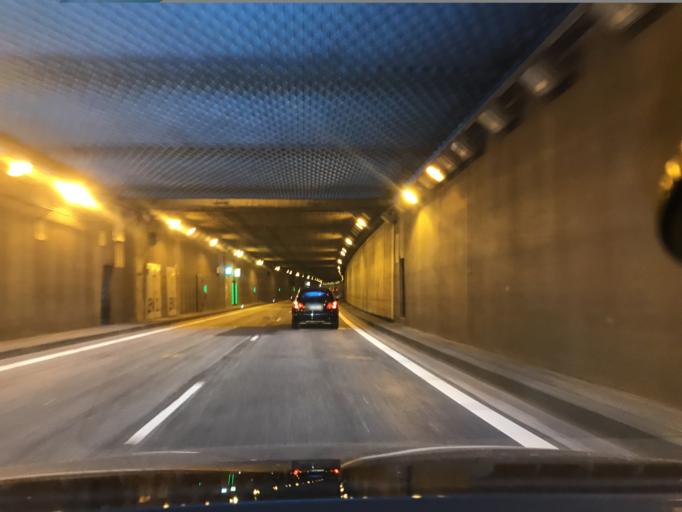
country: DE
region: North Rhine-Westphalia
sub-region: Regierungsbezirk Dusseldorf
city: Dusseldorf
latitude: 51.2306
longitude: 6.7383
